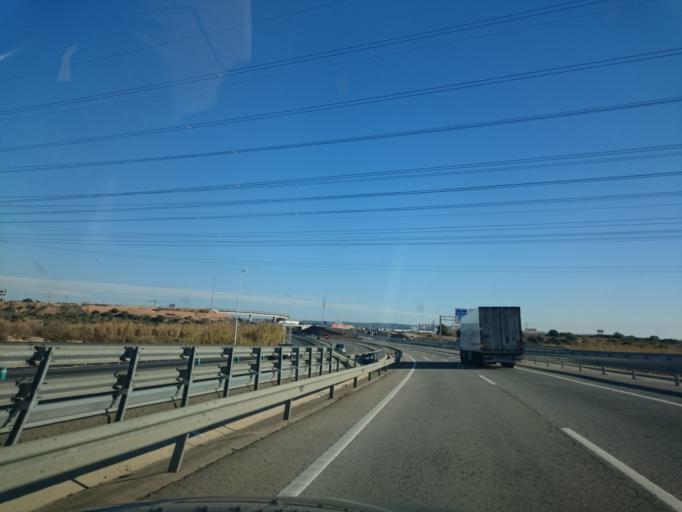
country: ES
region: Catalonia
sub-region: Provincia de Tarragona
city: Constanti
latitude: 41.1253
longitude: 1.1969
